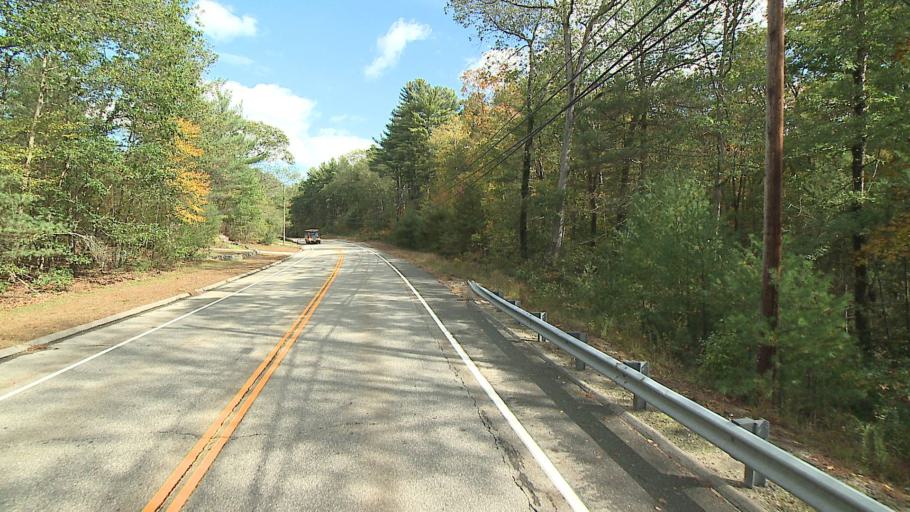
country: US
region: Connecticut
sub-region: Windham County
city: North Grosvenor Dale
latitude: 42.0067
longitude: -71.8946
